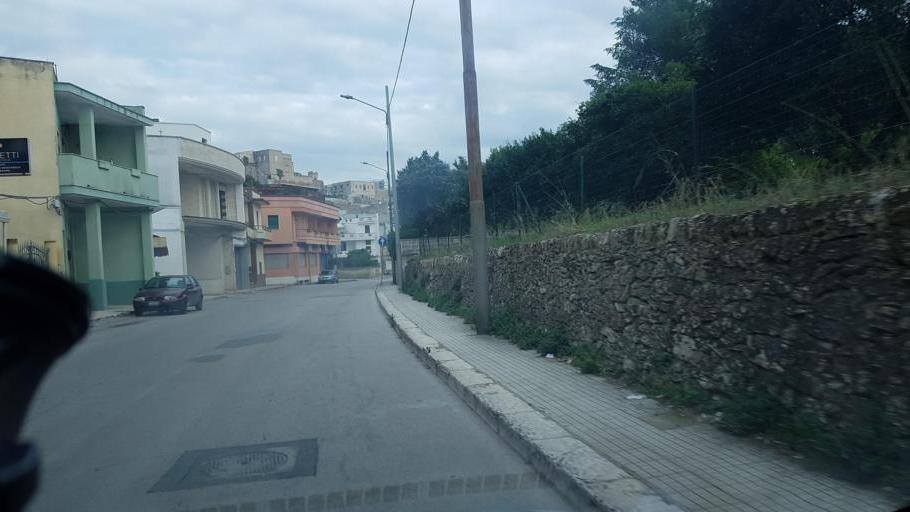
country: IT
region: Apulia
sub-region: Provincia di Brindisi
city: Oria
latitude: 40.5004
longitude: 17.6378
